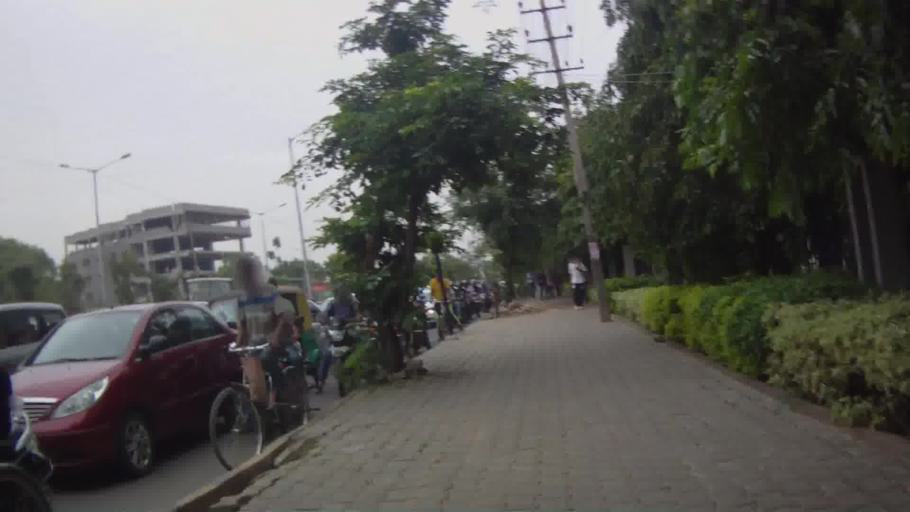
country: IN
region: Karnataka
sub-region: Bangalore Urban
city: Bangalore
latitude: 12.9813
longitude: 77.6939
